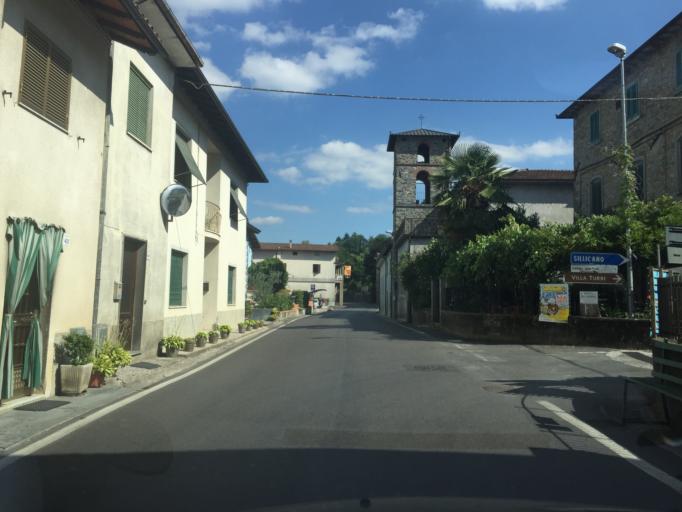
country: IT
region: Tuscany
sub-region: Provincia di Lucca
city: Villa Collemandina
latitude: 44.1354
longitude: 10.3698
